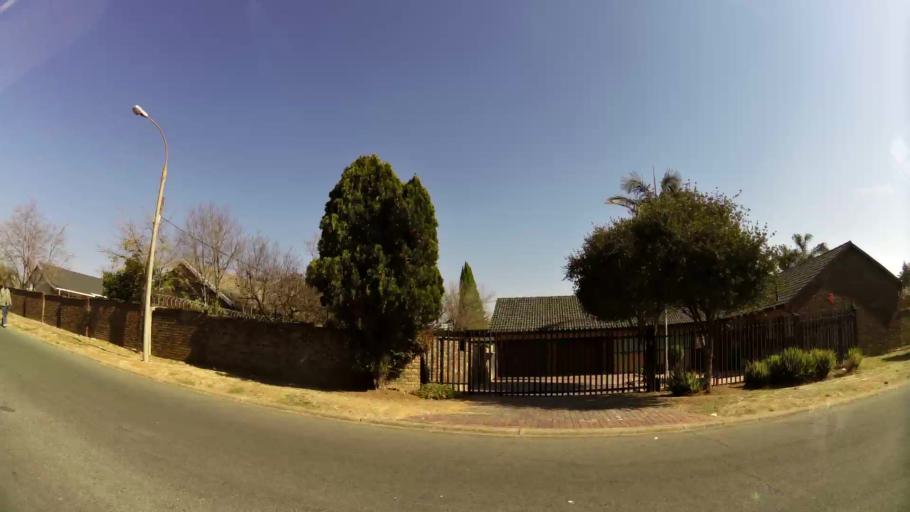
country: ZA
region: Gauteng
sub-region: Ekurhuleni Metropolitan Municipality
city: Tembisa
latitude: -26.0461
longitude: 28.2302
